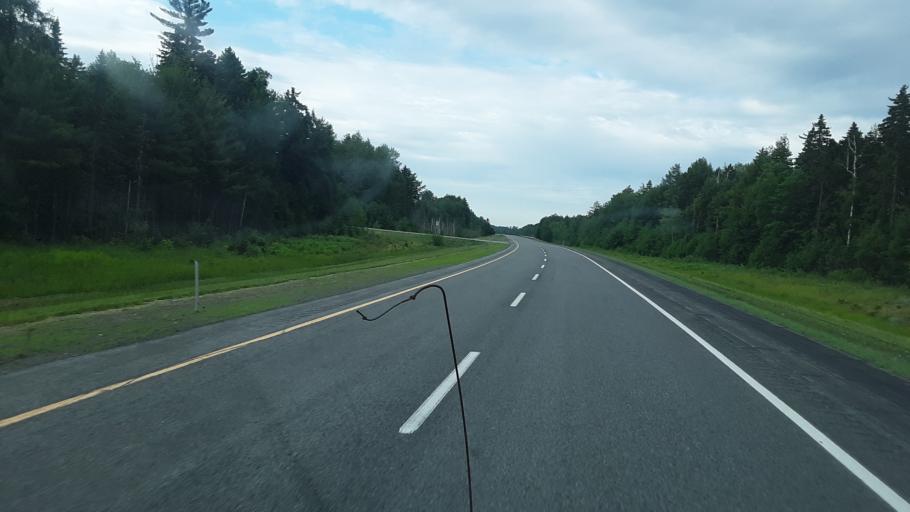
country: US
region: Maine
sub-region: Penobscot County
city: Medway
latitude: 45.7350
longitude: -68.4714
